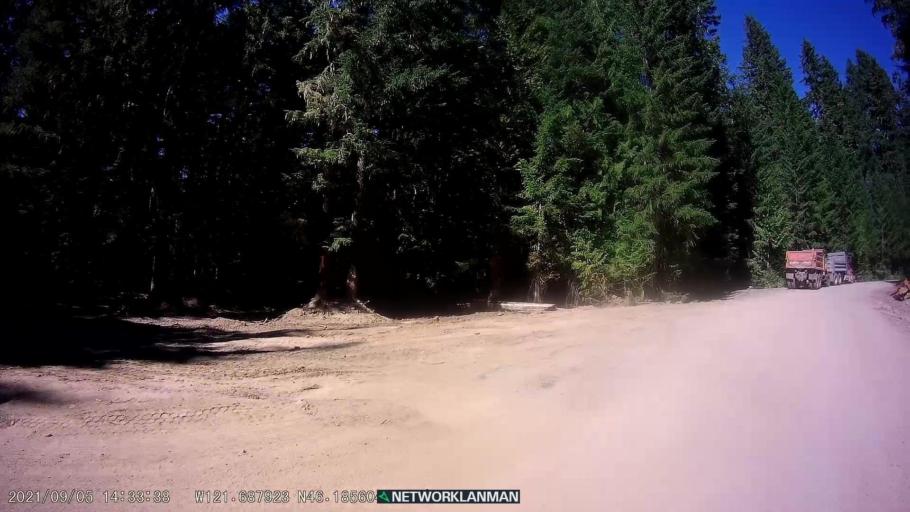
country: US
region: Washington
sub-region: Skamania County
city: Carson
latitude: 46.1856
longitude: -121.6880
